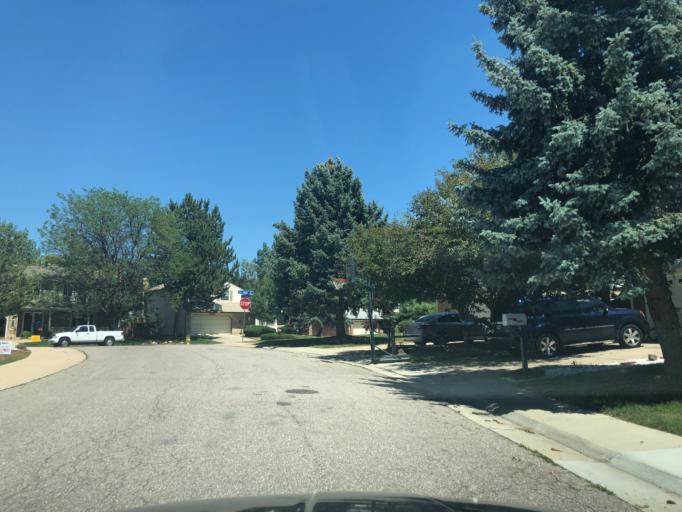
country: US
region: Colorado
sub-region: Arapahoe County
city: Dove Valley
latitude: 39.6162
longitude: -104.7860
